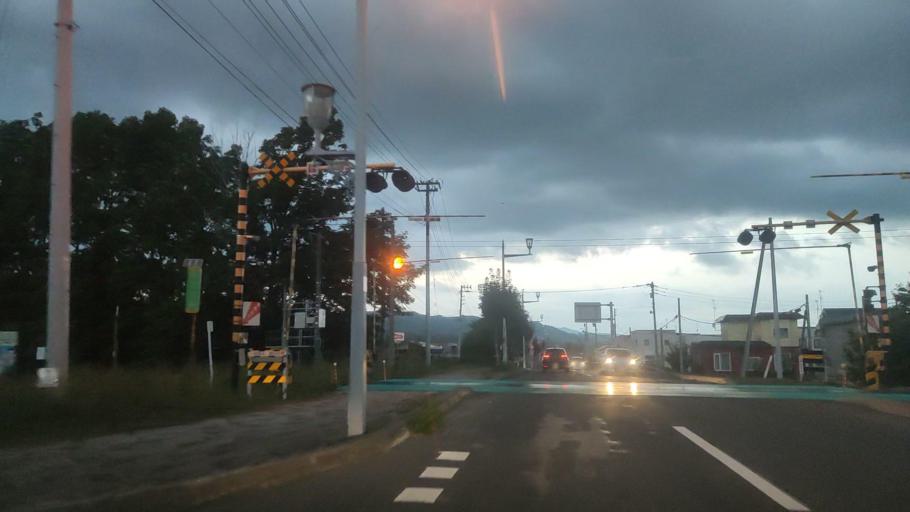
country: JP
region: Hokkaido
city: Shimo-furano
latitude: 43.3540
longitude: 142.3832
